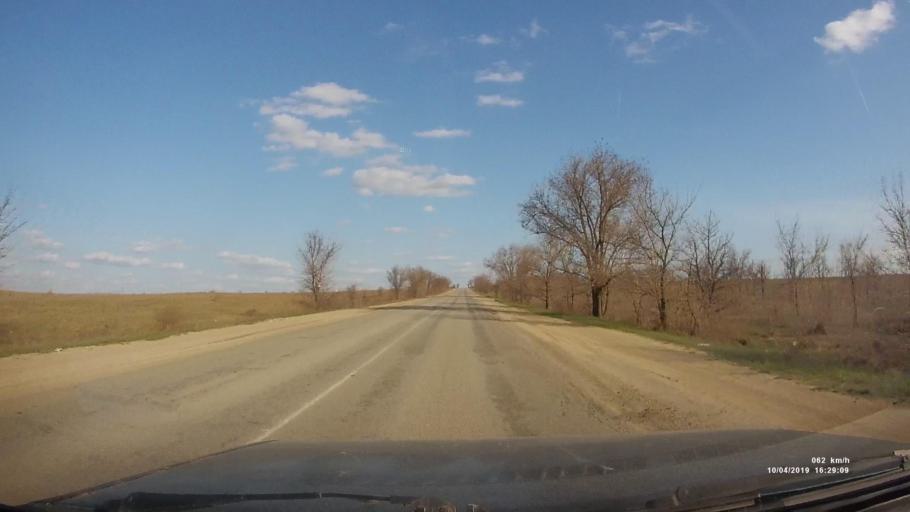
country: RU
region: Rostov
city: Staraya Stanitsa
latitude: 48.2701
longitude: 40.3519
